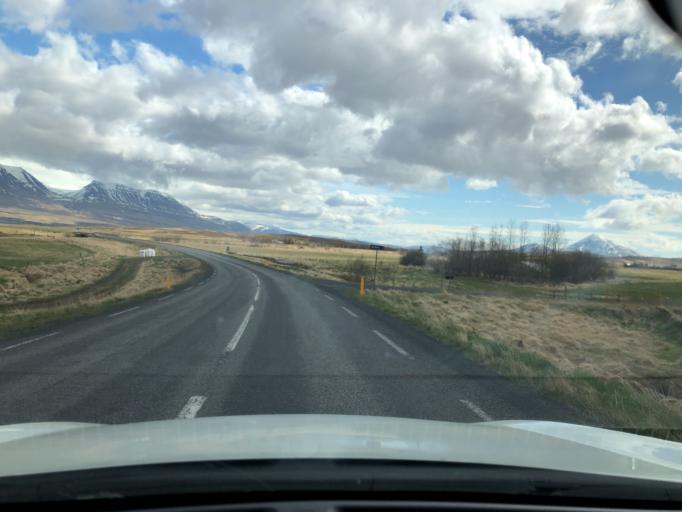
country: IS
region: Northwest
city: Saudarkrokur
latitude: 65.5454
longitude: -19.4730
